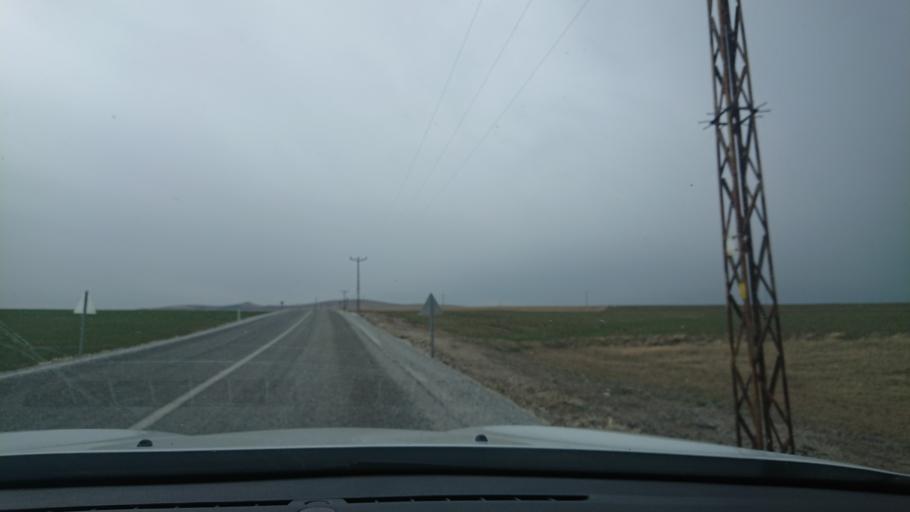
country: TR
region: Aksaray
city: Agacoren
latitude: 38.9231
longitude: 33.9438
